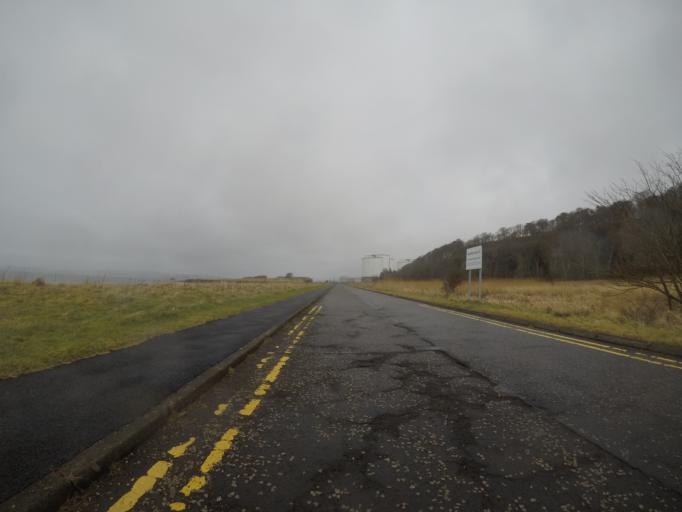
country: GB
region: Scotland
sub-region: North Ayrshire
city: Millport
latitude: 55.7155
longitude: -4.9025
